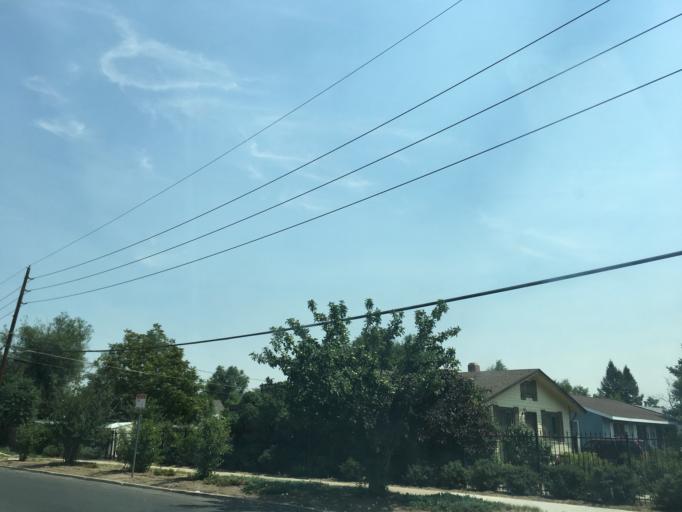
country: US
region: Colorado
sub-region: Jefferson County
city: Lakewood
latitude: 39.7086
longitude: -105.0299
